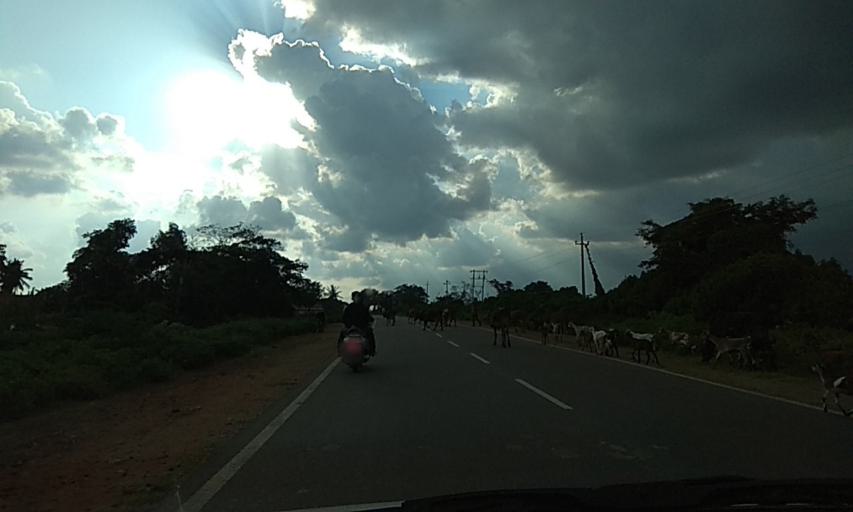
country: IN
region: Karnataka
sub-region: Chamrajnagar
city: Gundlupet
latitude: 11.8151
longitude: 76.7592
